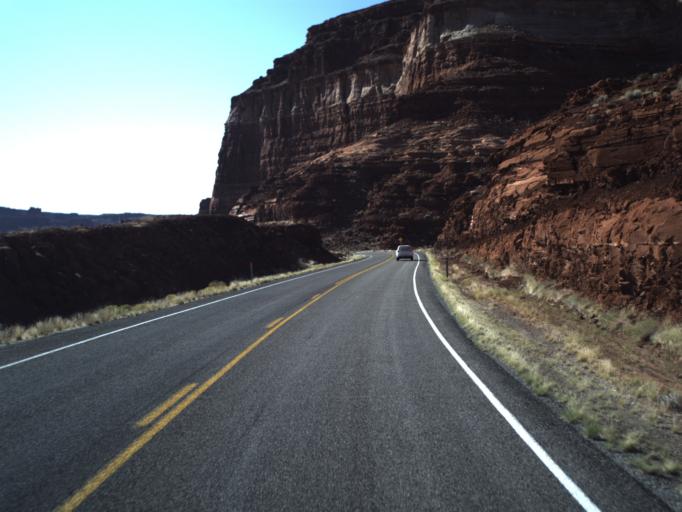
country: US
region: Utah
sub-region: San Juan County
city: Blanding
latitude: 37.9029
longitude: -110.3999
